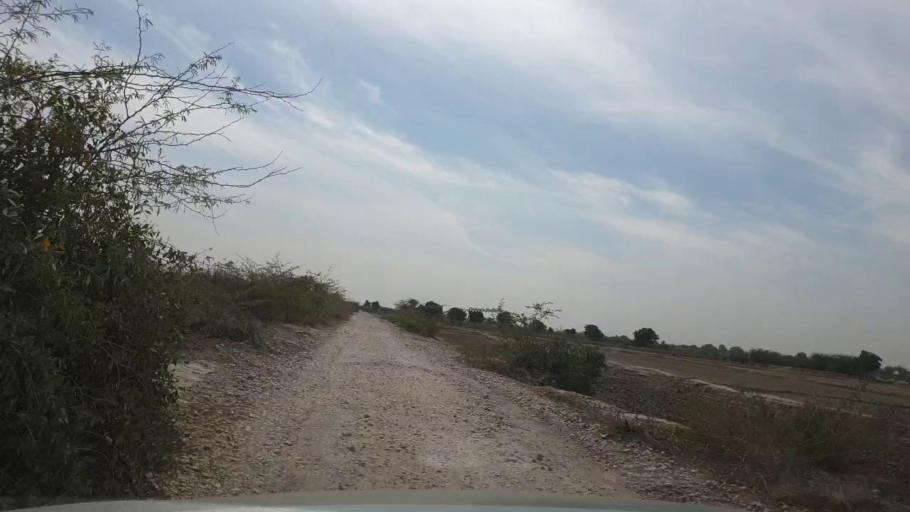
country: PK
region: Sindh
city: Nabisar
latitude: 25.0896
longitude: 69.5998
